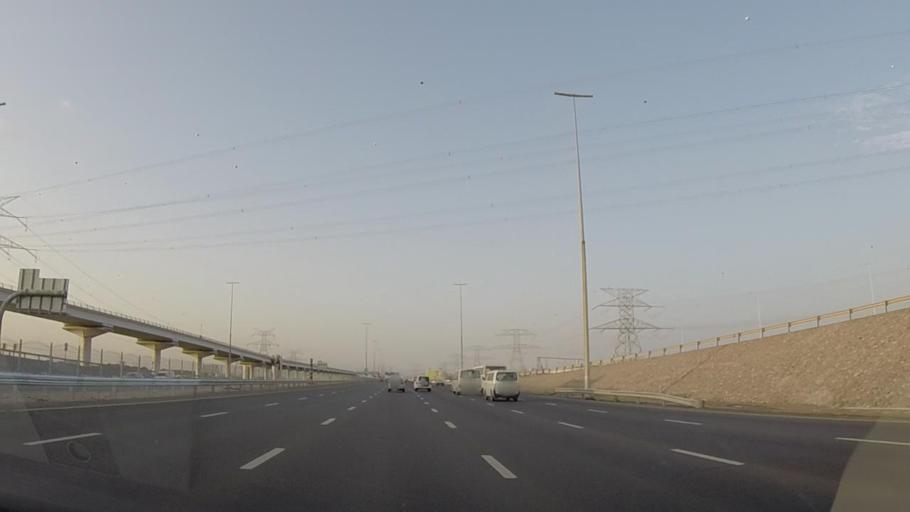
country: AE
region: Dubai
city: Dubai
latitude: 25.0393
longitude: 55.1102
